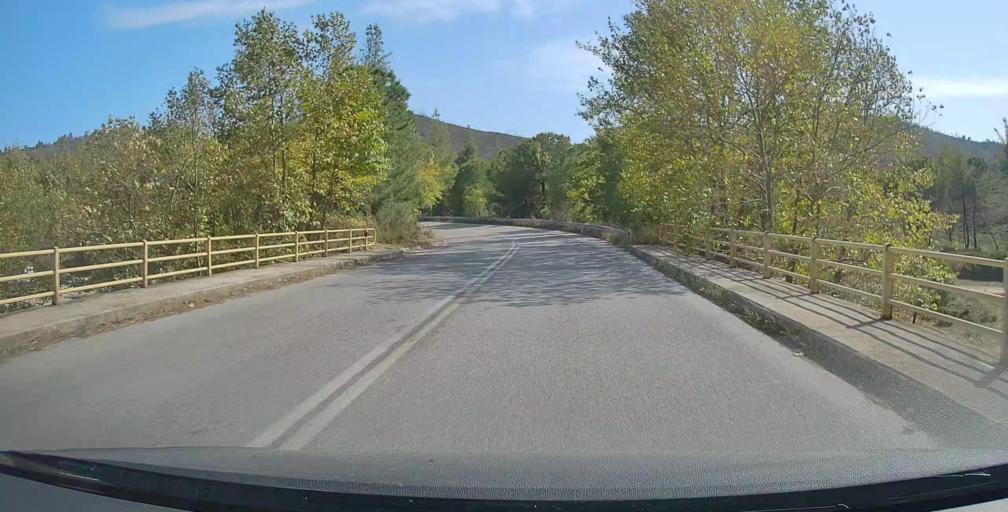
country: GR
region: Central Macedonia
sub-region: Nomos Chalkidikis
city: Sarti
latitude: 40.1175
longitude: 23.9710
